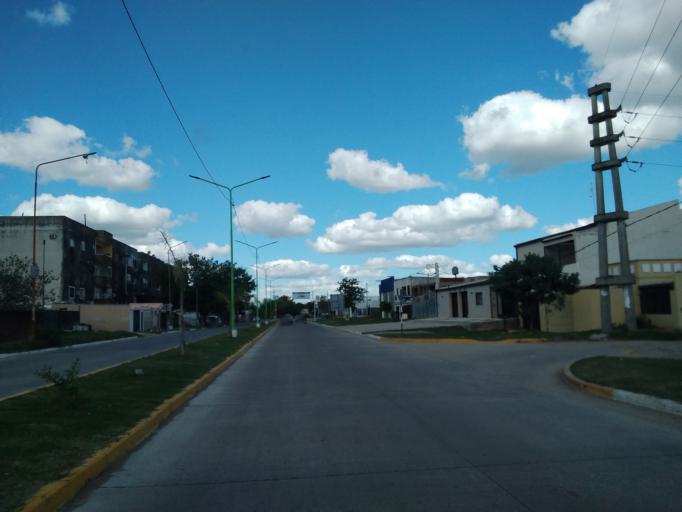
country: AR
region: Corrientes
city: Corrientes
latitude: -27.4992
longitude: -58.8272
